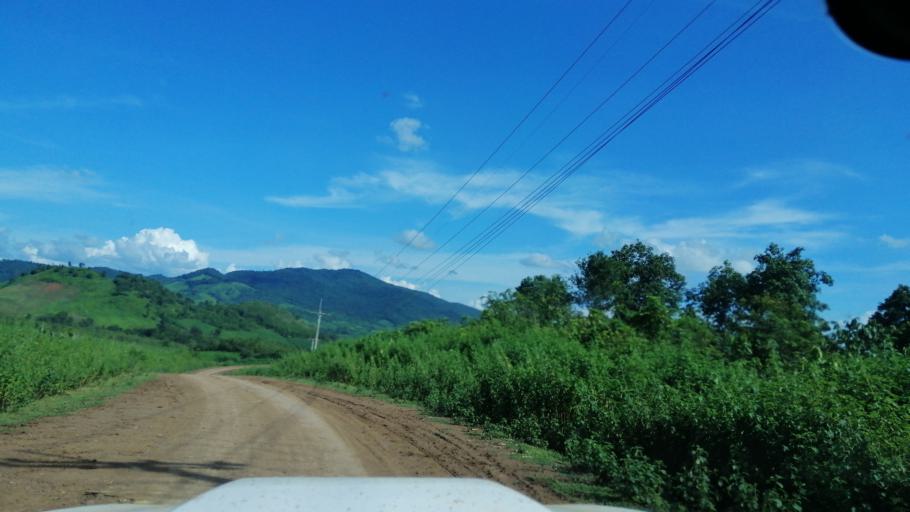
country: TH
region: Uttaradit
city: Ban Khok
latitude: 17.9095
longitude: 101.2029
